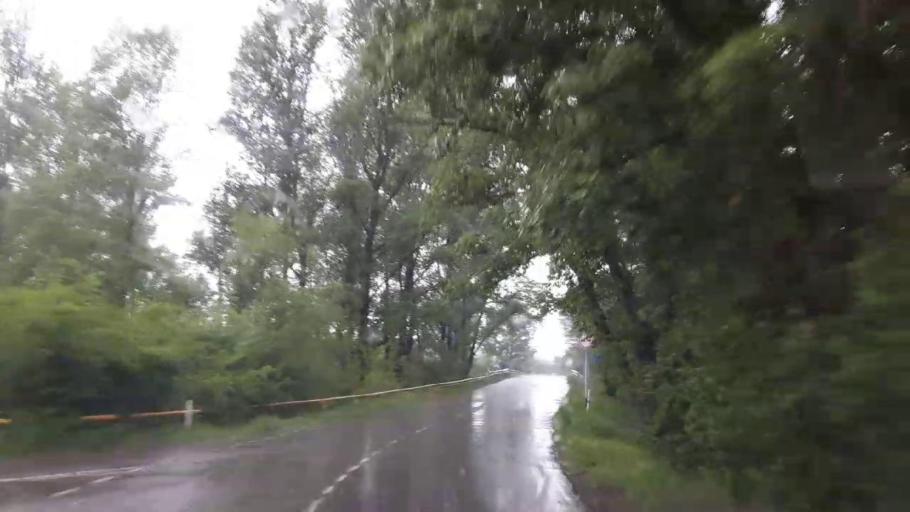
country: GE
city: Agara
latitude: 42.0122
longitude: 43.8536
